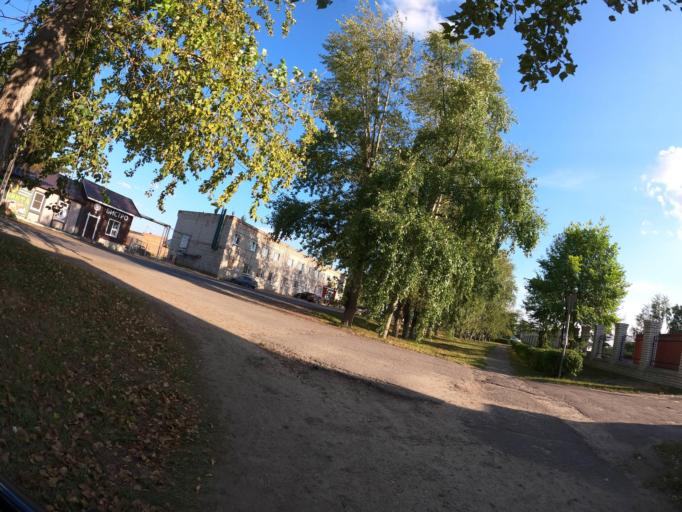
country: RU
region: Moskovskaya
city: Raduzhnyy
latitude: 55.1314
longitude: 38.7286
